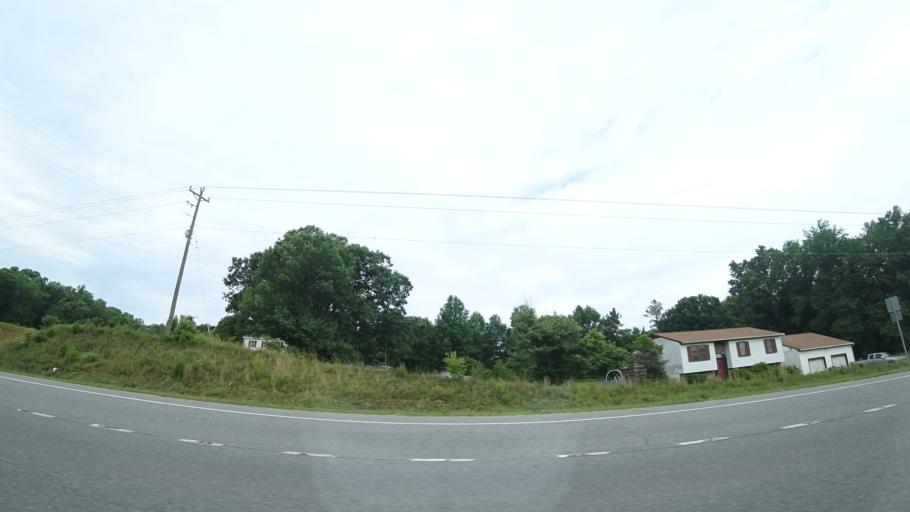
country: US
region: Virginia
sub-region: Spotsylvania County
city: Spotsylvania Courthouse
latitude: 38.1731
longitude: -77.6332
